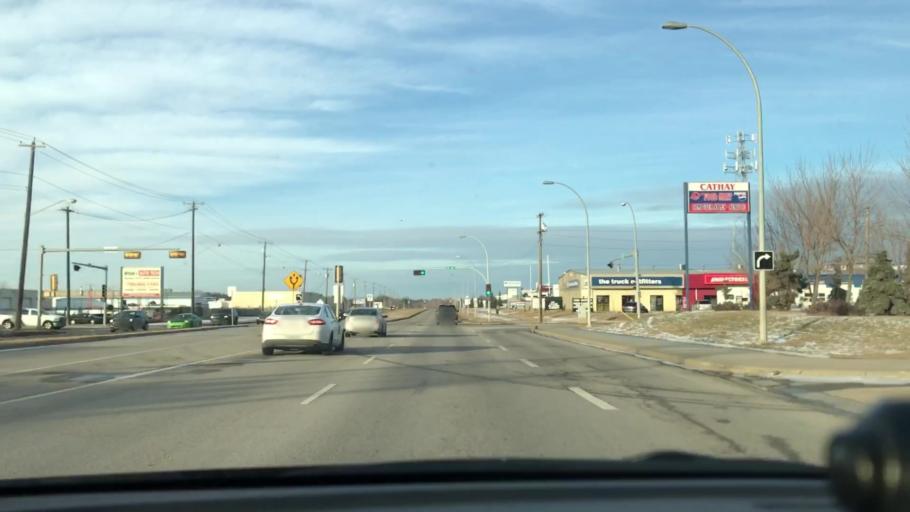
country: CA
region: Alberta
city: Edmonton
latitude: 53.4933
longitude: -113.4670
